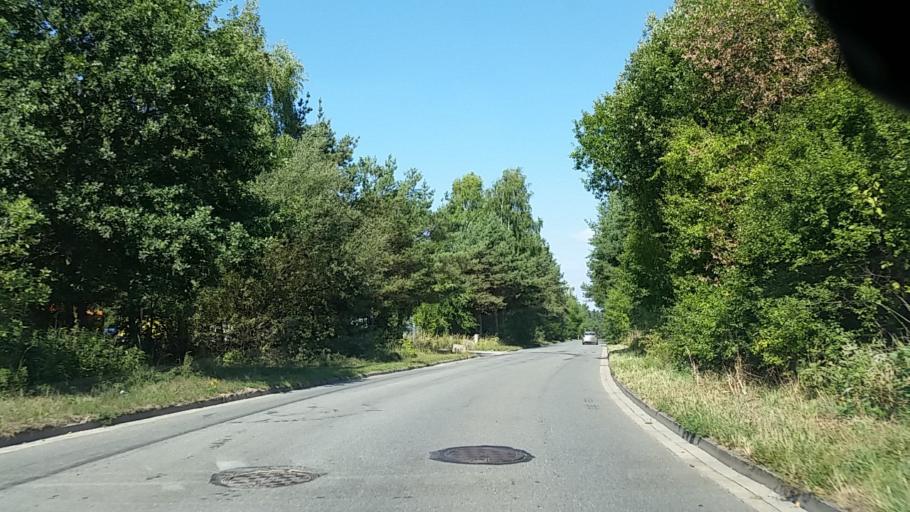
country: DE
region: Lower Saxony
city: Emmendorf
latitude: 52.9997
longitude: 10.5600
